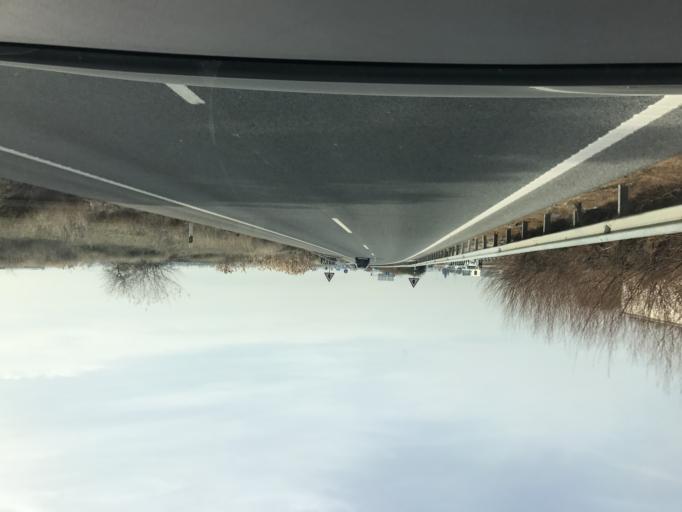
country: ES
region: Andalusia
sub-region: Provincia de Granada
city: Cijuela
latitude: 37.1944
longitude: -3.8030
